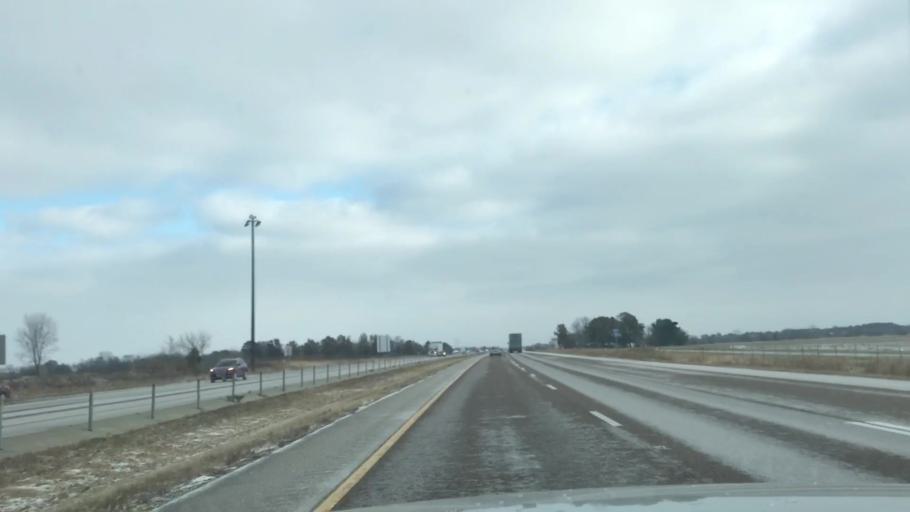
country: US
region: Illinois
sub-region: Madison County
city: Worden
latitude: 38.9336
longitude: -89.7989
